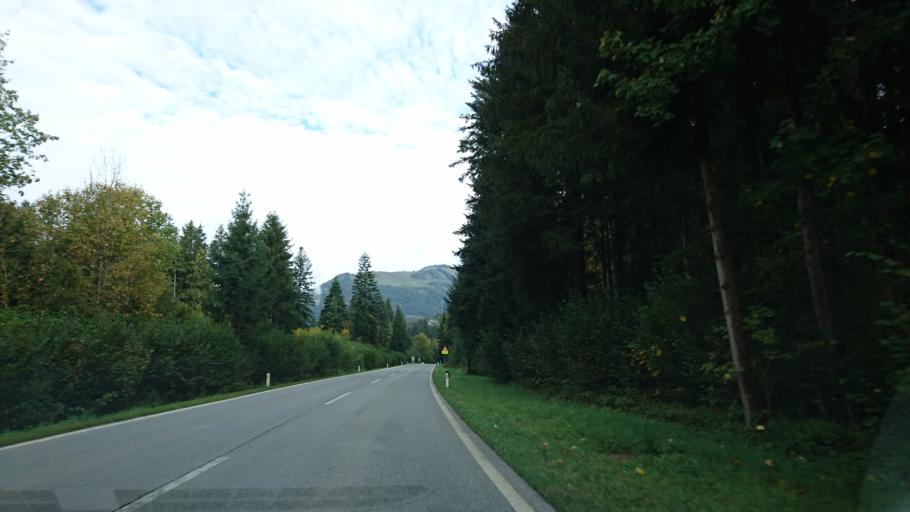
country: AT
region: Tyrol
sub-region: Politischer Bezirk Kitzbuhel
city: Kossen
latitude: 47.6585
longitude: 12.4256
